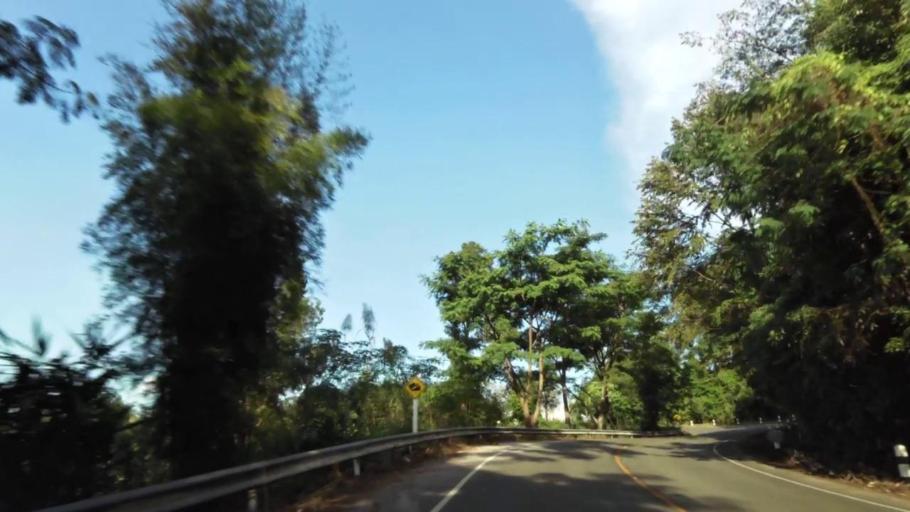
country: TH
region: Chiang Rai
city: Khun Tan
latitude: 19.8623
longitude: 100.4281
